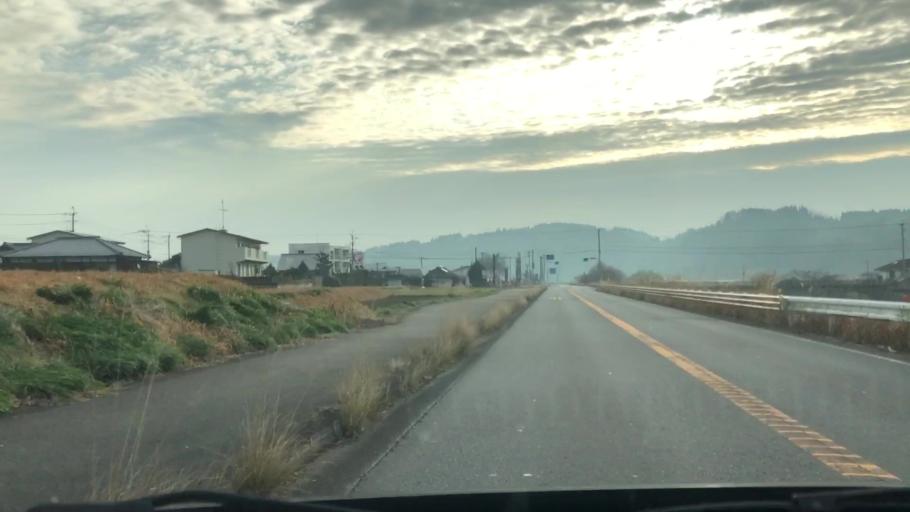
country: JP
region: Oita
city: Takedamachi
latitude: 32.9670
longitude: 131.4795
